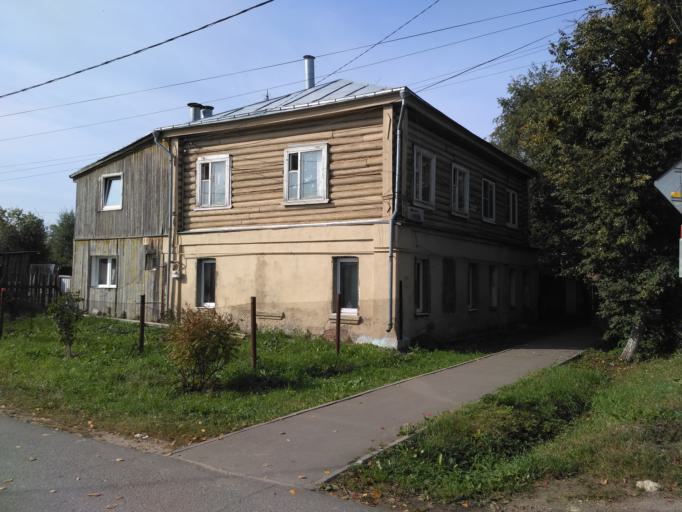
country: RU
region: Moskovskaya
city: Sergiyev Posad
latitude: 56.3085
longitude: 38.1141
